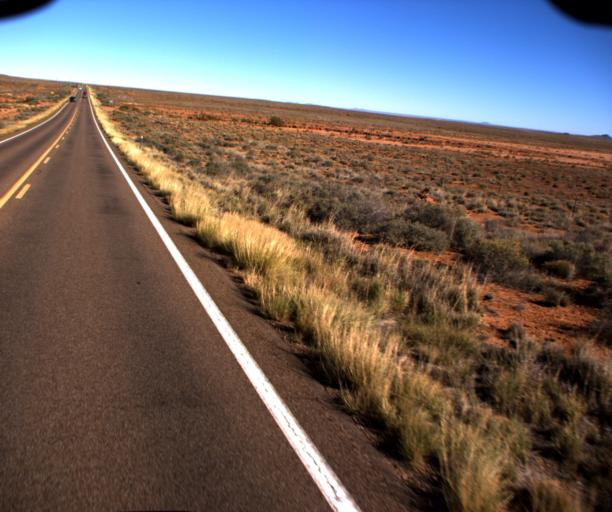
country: US
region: Arizona
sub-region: Navajo County
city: Holbrook
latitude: 34.7131
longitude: -110.1120
